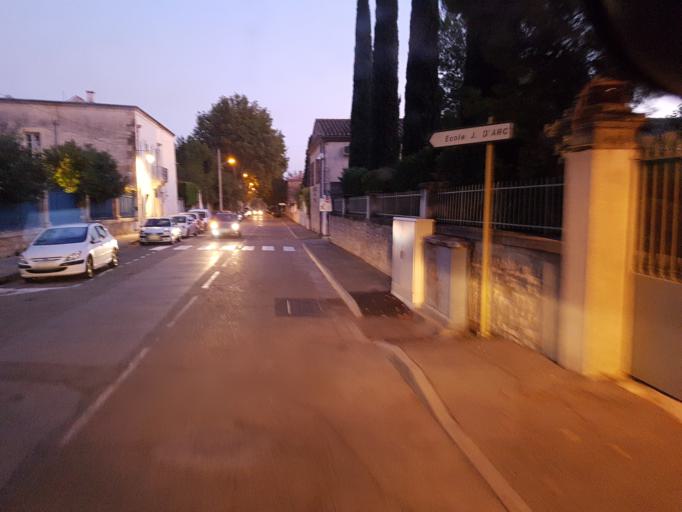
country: FR
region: Languedoc-Roussillon
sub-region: Departement du Gard
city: Bellegarde
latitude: 43.7533
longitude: 4.5157
